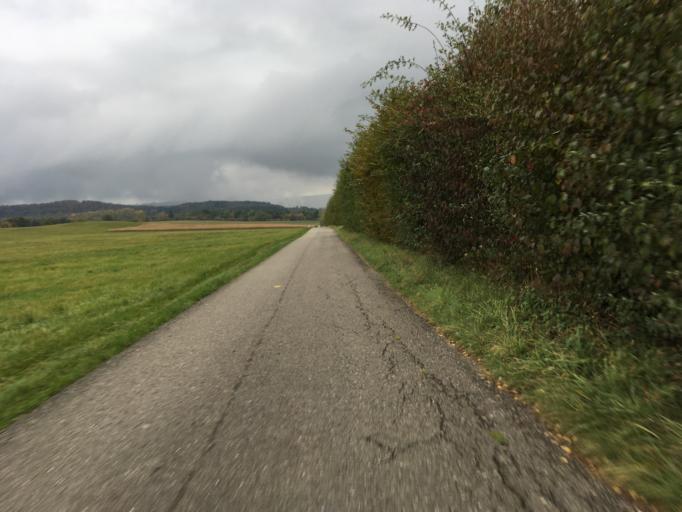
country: DE
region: Baden-Wuerttemberg
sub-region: Tuebingen Region
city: Nehren
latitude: 48.4383
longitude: 9.0831
